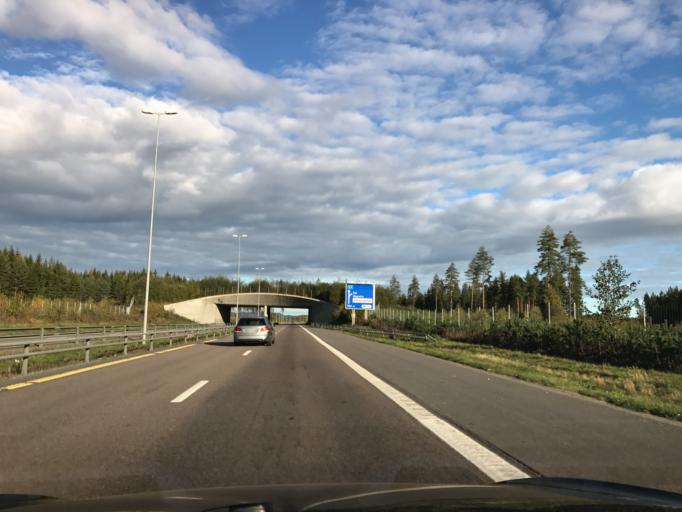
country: NO
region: Akershus
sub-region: Eidsvoll
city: Raholt
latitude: 60.2219
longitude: 11.1786
